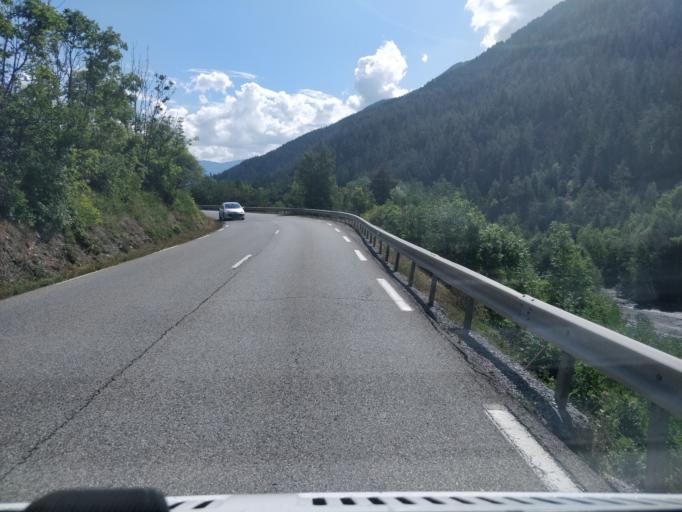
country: FR
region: Provence-Alpes-Cote d'Azur
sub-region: Departement des Alpes-de-Haute-Provence
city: Barcelonnette
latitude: 44.4009
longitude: 6.5161
